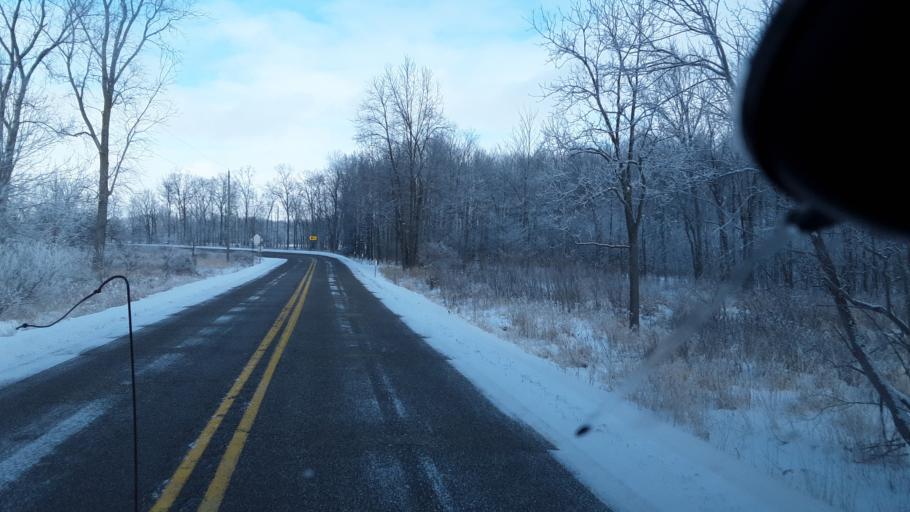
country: US
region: Michigan
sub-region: Eaton County
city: Eaton Rapids
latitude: 42.4928
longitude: -84.6256
